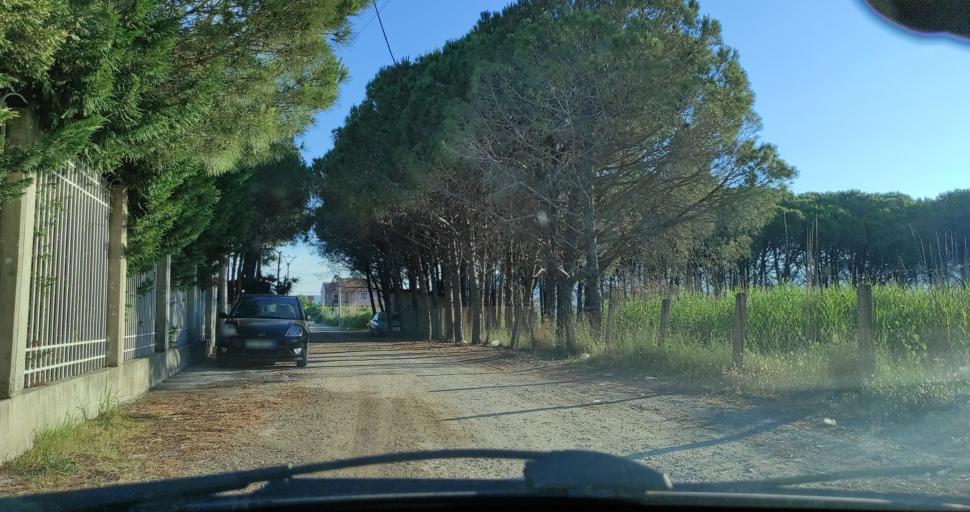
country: AL
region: Shkoder
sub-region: Rrethi i Shkodres
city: Velipoje
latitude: 41.8611
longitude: 19.4376
